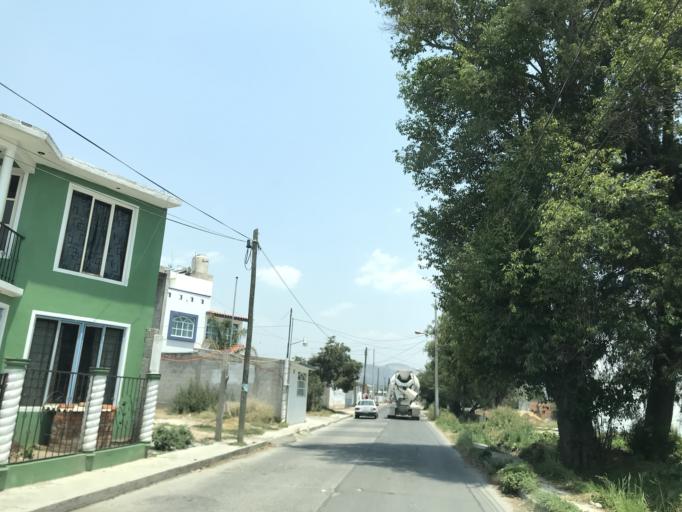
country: MX
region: Tlaxcala
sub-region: Ixtacuixtla de Mariano Matamoros
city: Villa Mariano Matamoros
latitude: 19.3139
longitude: -98.3727
